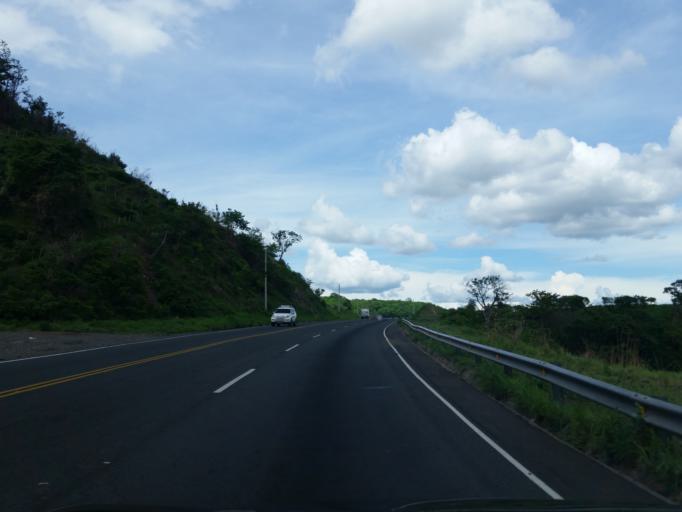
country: NI
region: Managua
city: Valle San Francisco
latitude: 12.4932
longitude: -86.0631
